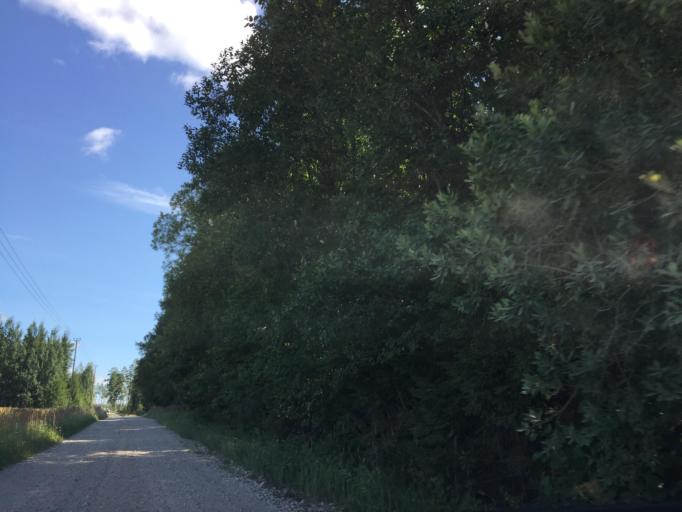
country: LV
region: Talsu Rajons
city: Stende
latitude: 57.1794
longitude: 22.3142
